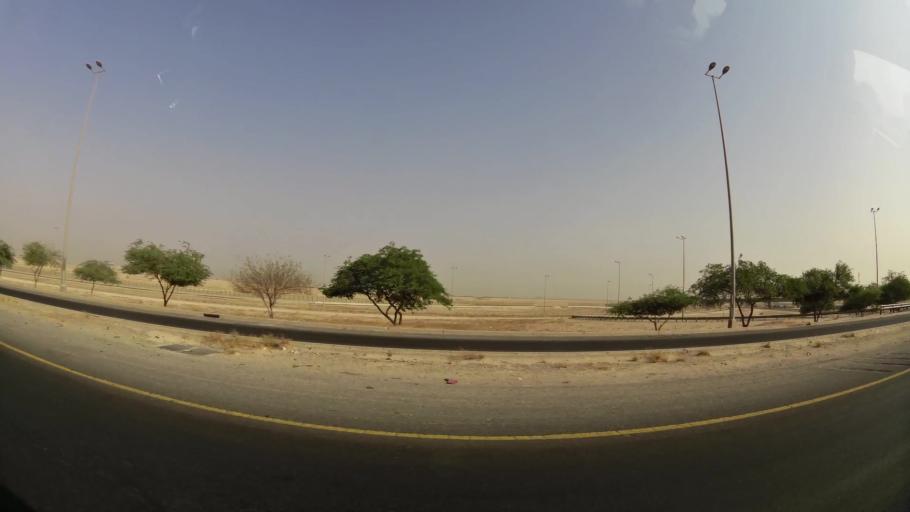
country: KW
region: Al Farwaniyah
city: Janub as Surrah
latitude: 29.1800
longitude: 47.9893
